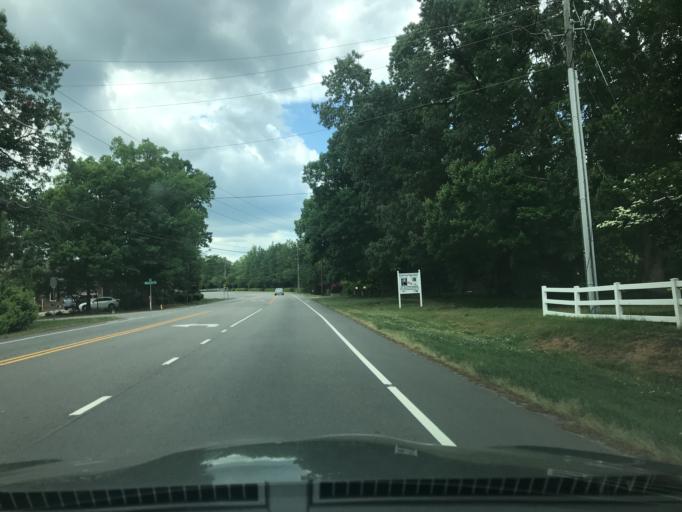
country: US
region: North Carolina
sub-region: Wake County
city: Wake Forest
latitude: 35.9001
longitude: -78.6005
